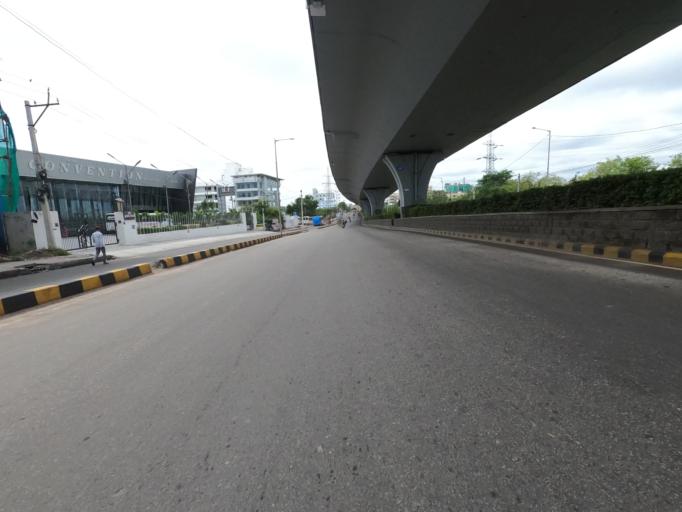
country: IN
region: Telangana
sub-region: Hyderabad
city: Hyderabad
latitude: 17.3409
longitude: 78.4242
